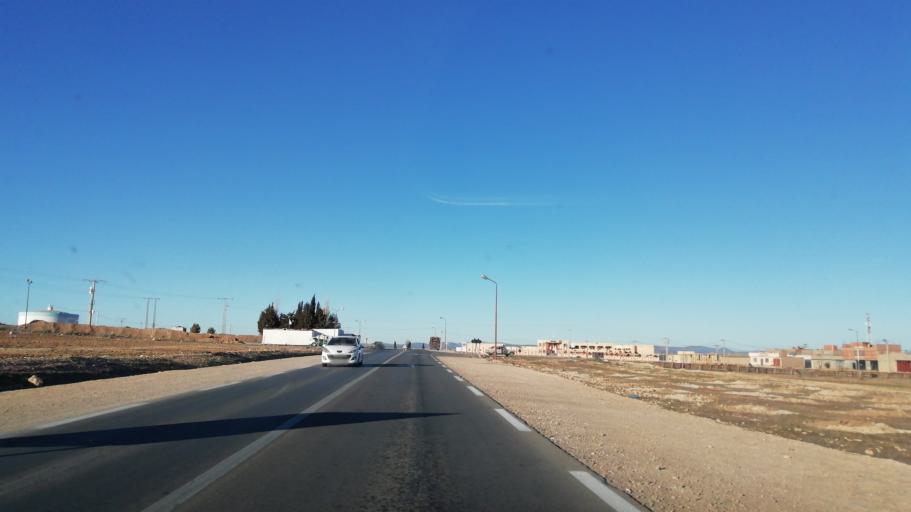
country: DZ
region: Tlemcen
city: Sebdou
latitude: 34.4778
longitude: -1.2711
